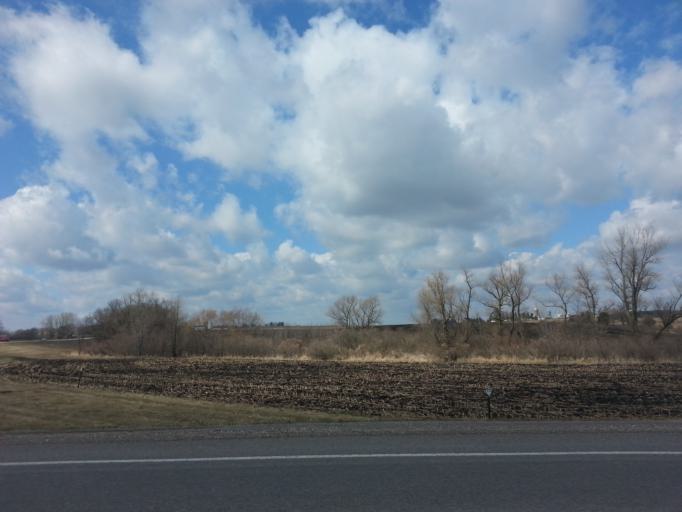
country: US
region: Minnesota
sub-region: Dodge County
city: Mantorville
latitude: 44.0801
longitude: -92.7595
